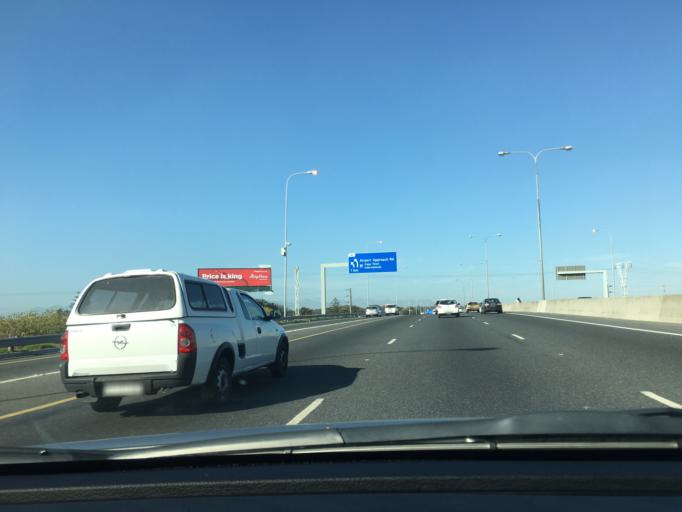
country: ZA
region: Western Cape
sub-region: City of Cape Town
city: Lansdowne
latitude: -33.9613
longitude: 18.5609
